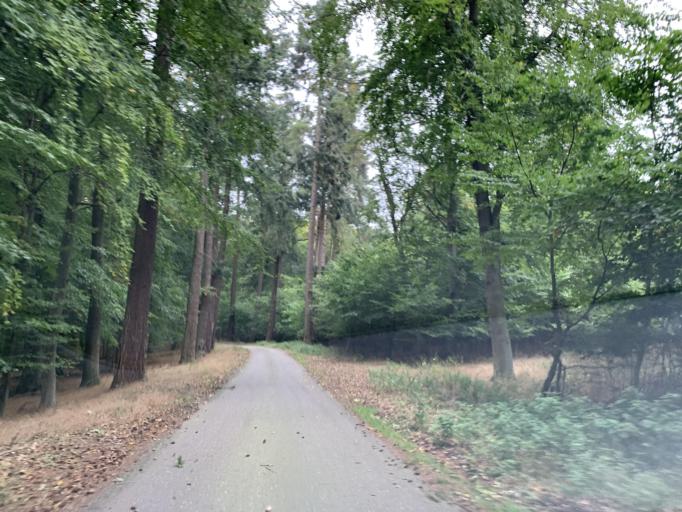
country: DE
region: Mecklenburg-Vorpommern
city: Woldegk
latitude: 53.3208
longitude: 13.6092
